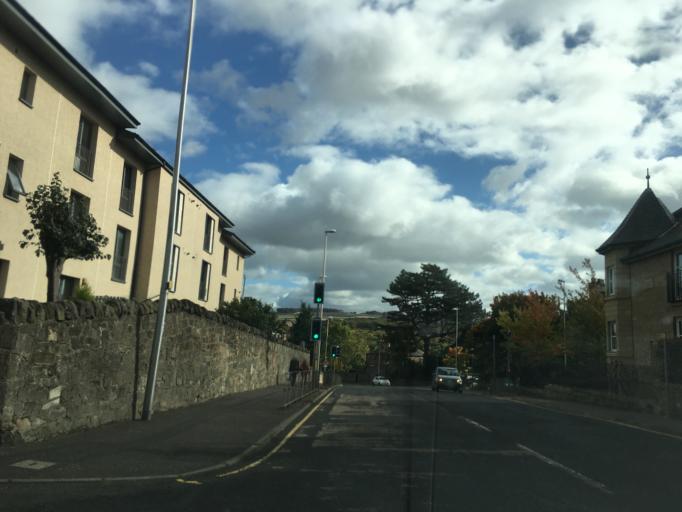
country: GB
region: Scotland
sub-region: Midlothian
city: Dalkeith
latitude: 55.8927
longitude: -3.0680
